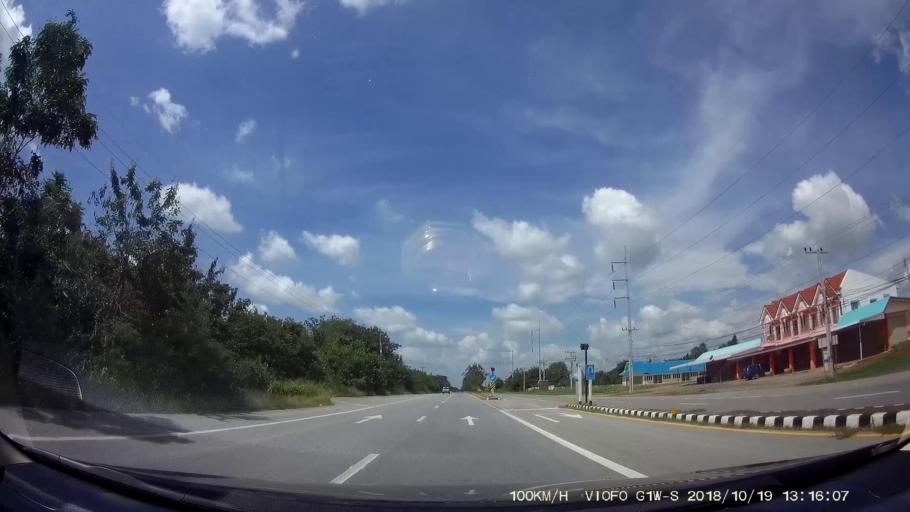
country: TH
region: Chaiyaphum
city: Chatturat
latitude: 15.3992
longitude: 101.8379
